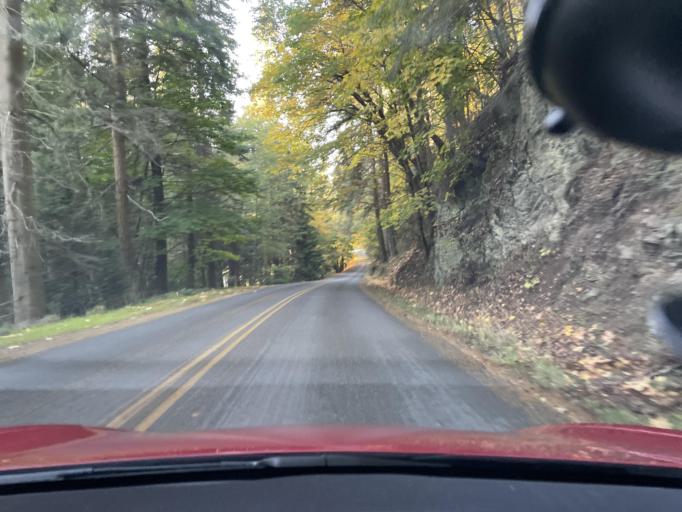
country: US
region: Washington
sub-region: San Juan County
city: Friday Harbor
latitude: 48.5389
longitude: -123.1584
